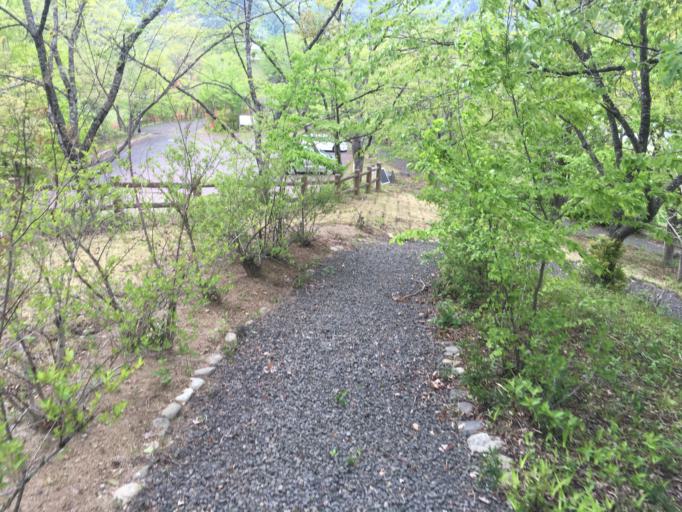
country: JP
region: Miyagi
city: Marumori
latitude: 37.7198
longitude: 140.8288
